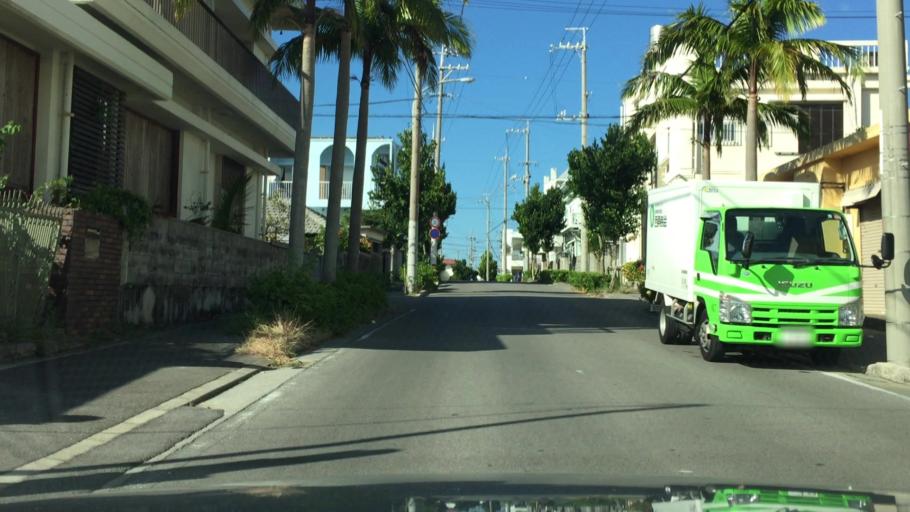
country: JP
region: Okinawa
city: Ishigaki
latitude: 24.3450
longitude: 124.1604
